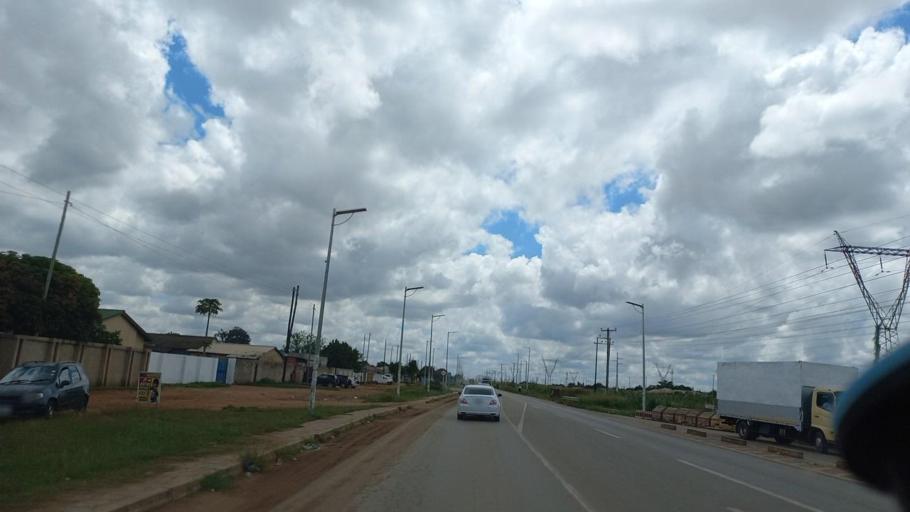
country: ZM
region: Lusaka
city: Lusaka
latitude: -15.4565
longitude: 28.3282
